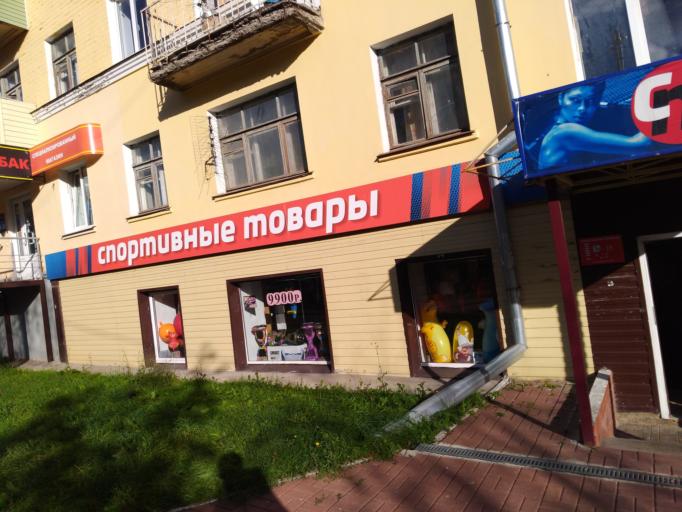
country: RU
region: Kaluga
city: Kaluga
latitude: 54.5276
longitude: 36.2735
